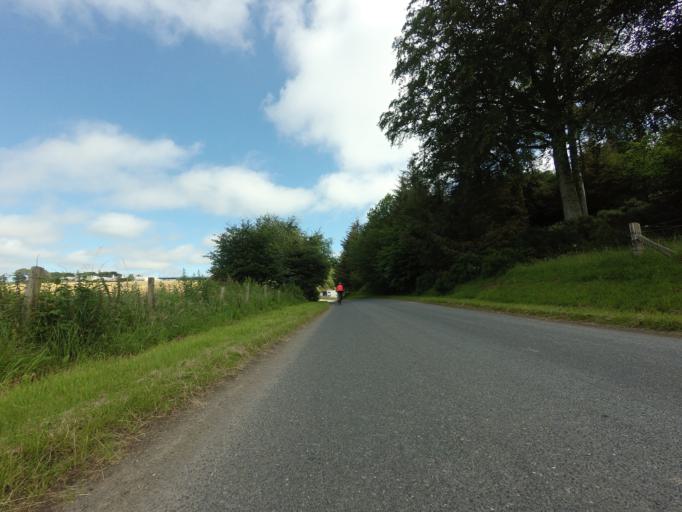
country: GB
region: Scotland
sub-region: Aberdeenshire
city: Turriff
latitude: 57.5643
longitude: -2.4934
